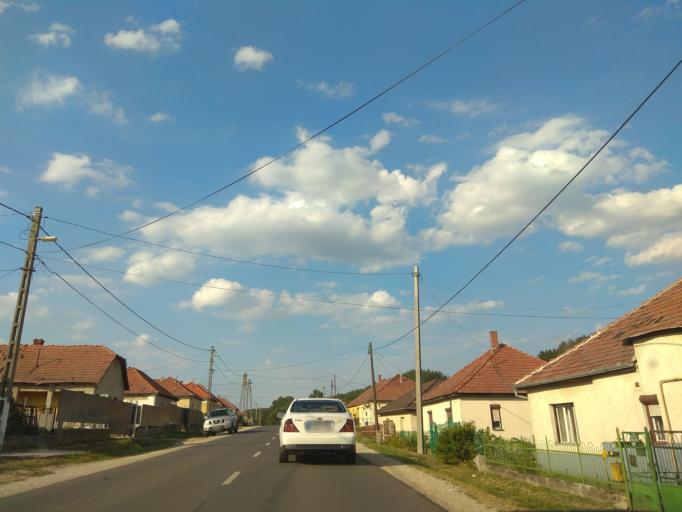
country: HU
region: Borsod-Abauj-Zemplen
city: Harsany
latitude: 47.9745
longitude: 20.7423
